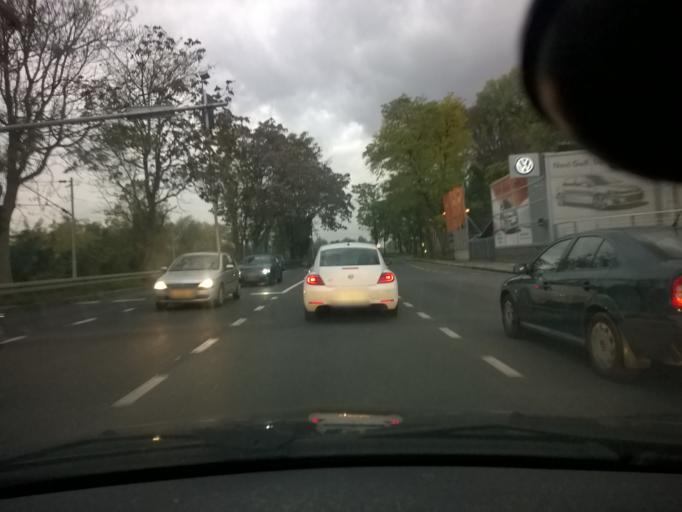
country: HR
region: Zagrebacka
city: Bestovje
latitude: 45.8177
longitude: 15.8311
